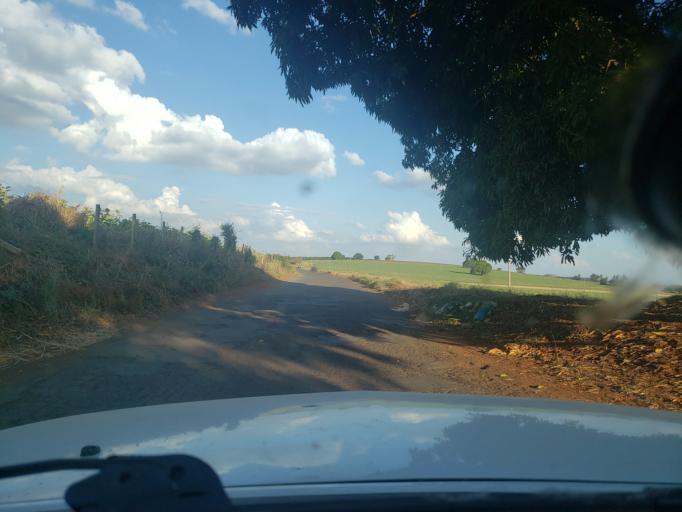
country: BR
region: Sao Paulo
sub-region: Mogi-Mirim
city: Mogi Mirim
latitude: -22.4664
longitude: -46.9324
